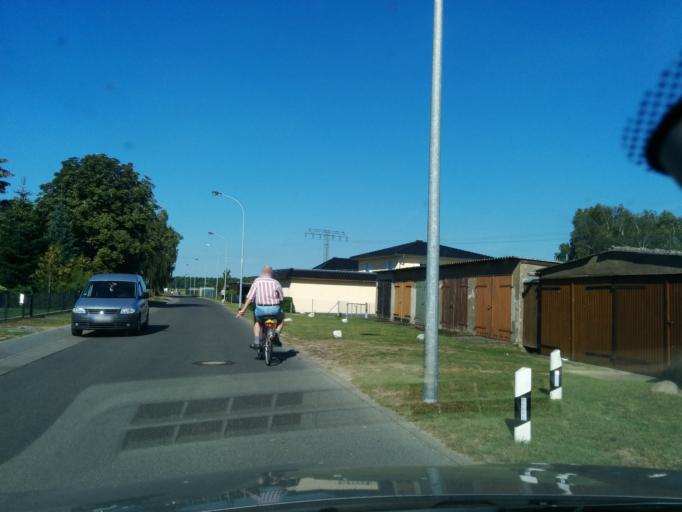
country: DE
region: Mecklenburg-Vorpommern
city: Torgelow
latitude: 53.6376
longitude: 14.0240
